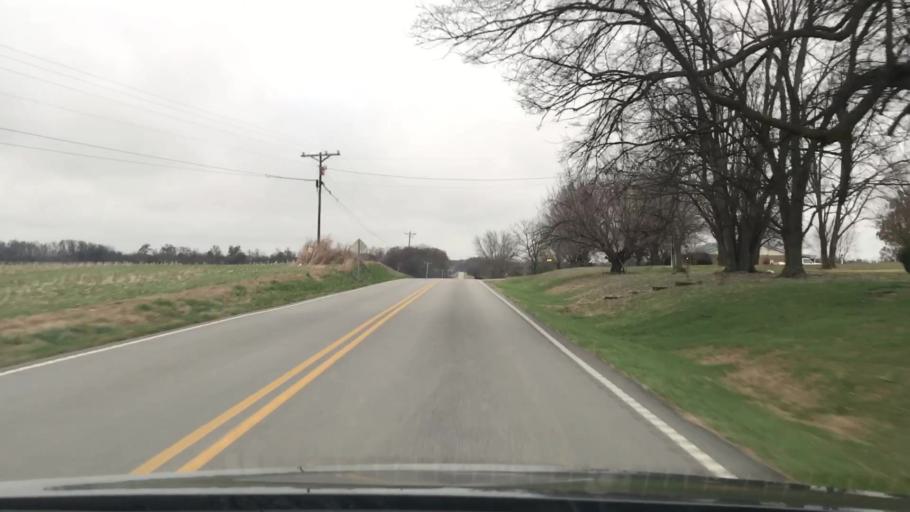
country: US
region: Kentucky
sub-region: Todd County
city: Guthrie
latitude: 36.7091
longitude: -87.1941
